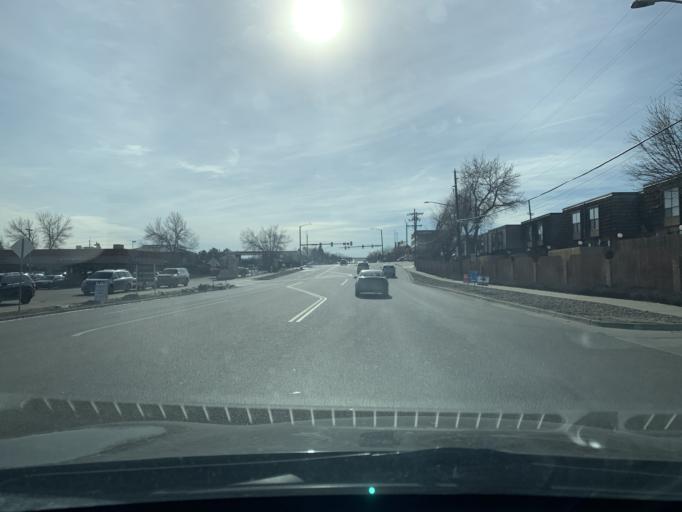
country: US
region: Colorado
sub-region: Jefferson County
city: Arvada
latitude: 39.8144
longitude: -105.1380
